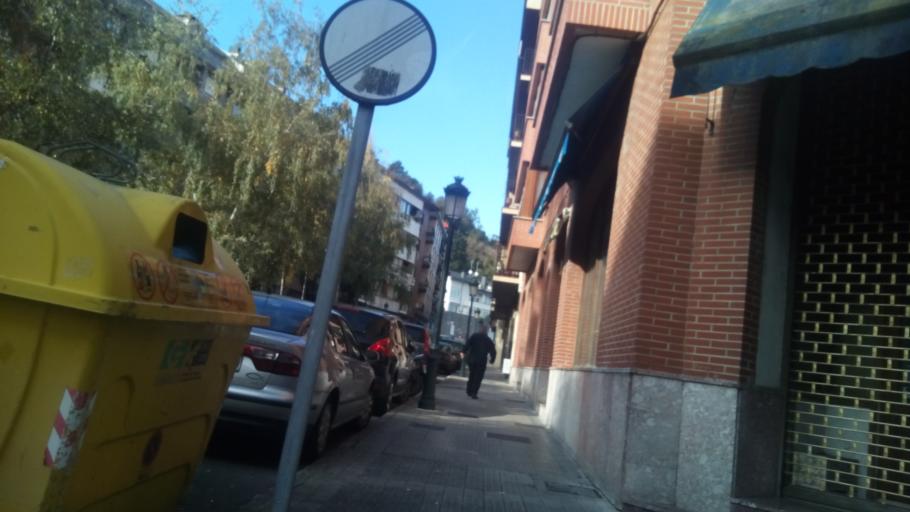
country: ES
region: Basque Country
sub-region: Bizkaia
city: Gernika-Lumo
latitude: 43.3161
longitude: -2.6793
